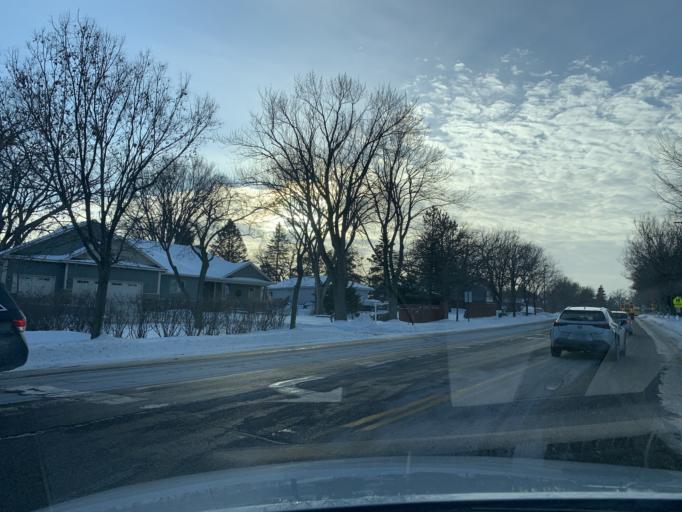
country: US
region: Minnesota
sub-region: Hennepin County
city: Minnetonka Mills
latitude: 44.9550
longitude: -93.3960
